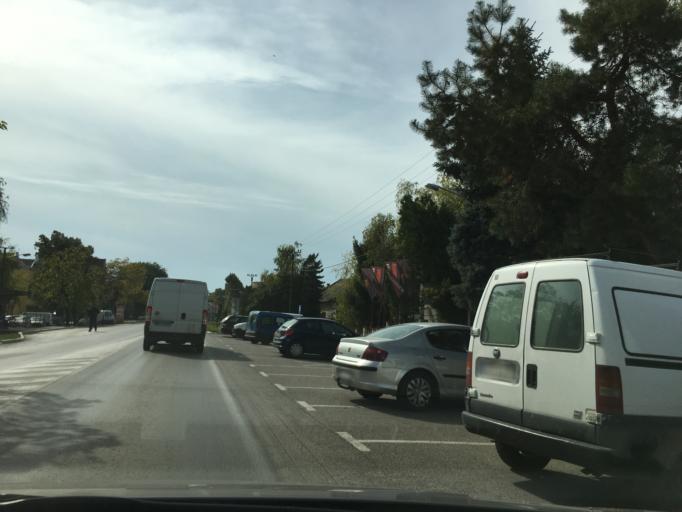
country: RS
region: Autonomna Pokrajina Vojvodina
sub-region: Juznobacki Okrug
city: Temerin
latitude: 45.4062
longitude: 19.8871
